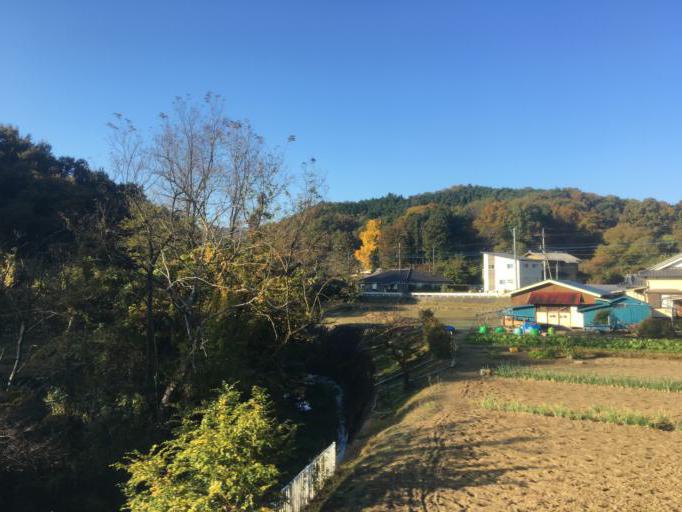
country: JP
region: Saitama
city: Yorii
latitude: 36.0918
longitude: 139.1978
